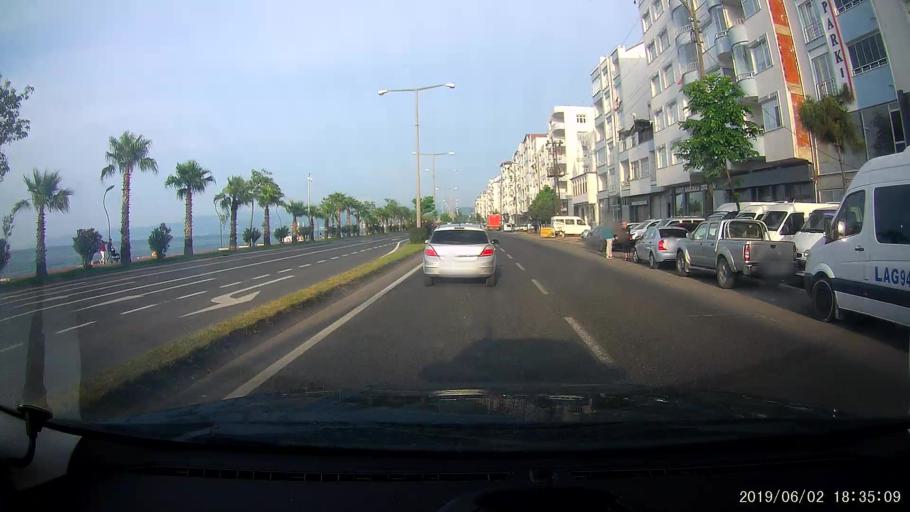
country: TR
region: Ordu
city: Fatsa
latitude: 41.0271
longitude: 37.5115
